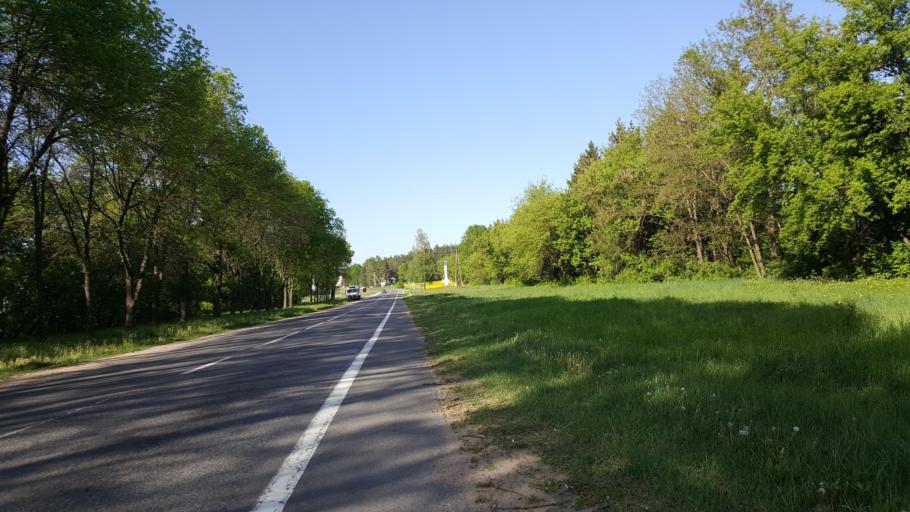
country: BY
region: Brest
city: Kamyanyets
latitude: 52.3862
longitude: 23.8158
